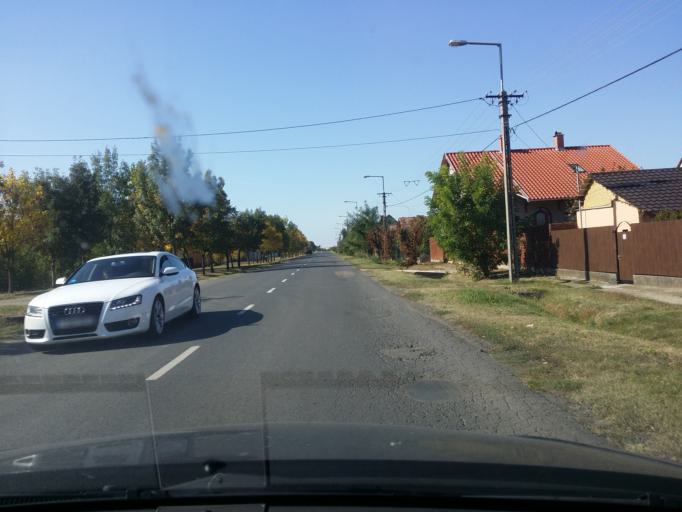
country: HU
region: Jasz-Nagykun-Szolnok
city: Mezotur
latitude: 47.0025
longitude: 20.5986
